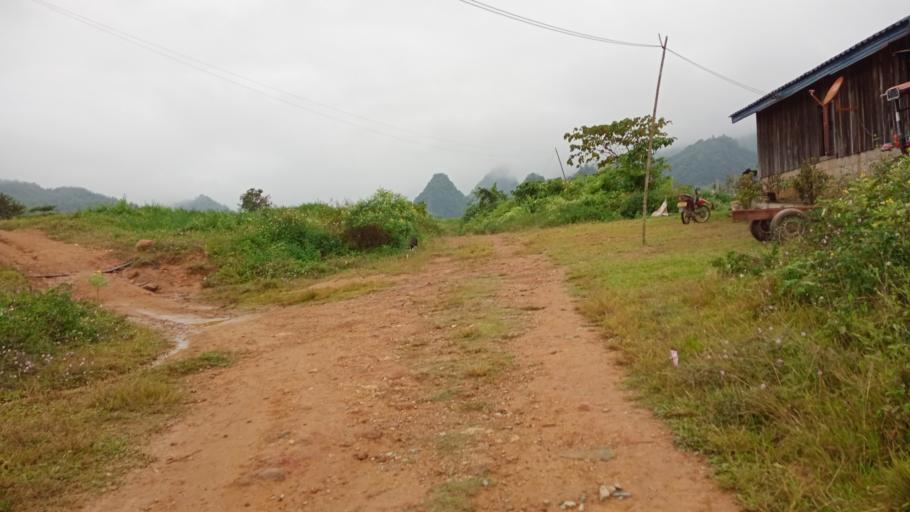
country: LA
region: Xiangkhoang
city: Phonsavan
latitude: 19.1028
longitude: 102.9287
